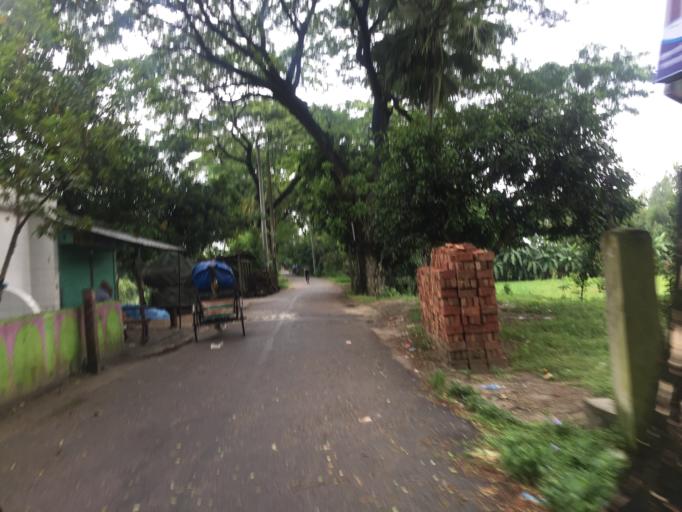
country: BD
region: Dhaka
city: Narayanganj
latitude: 23.5316
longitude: 90.4712
